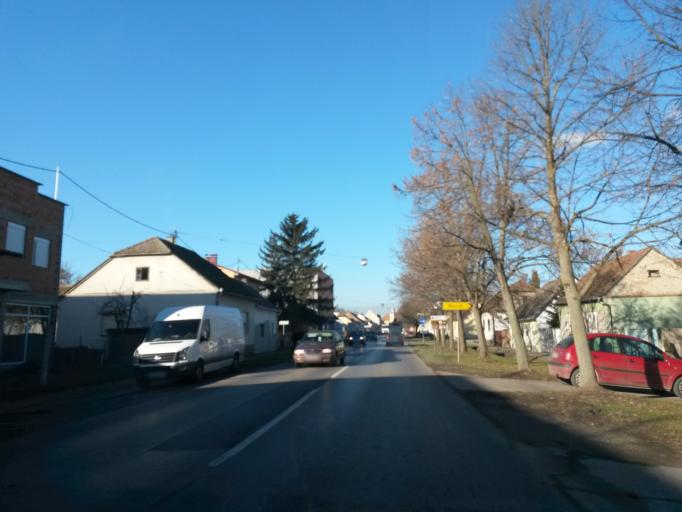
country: HR
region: Osjecko-Baranjska
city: Valpovo
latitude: 45.6556
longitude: 18.4242
